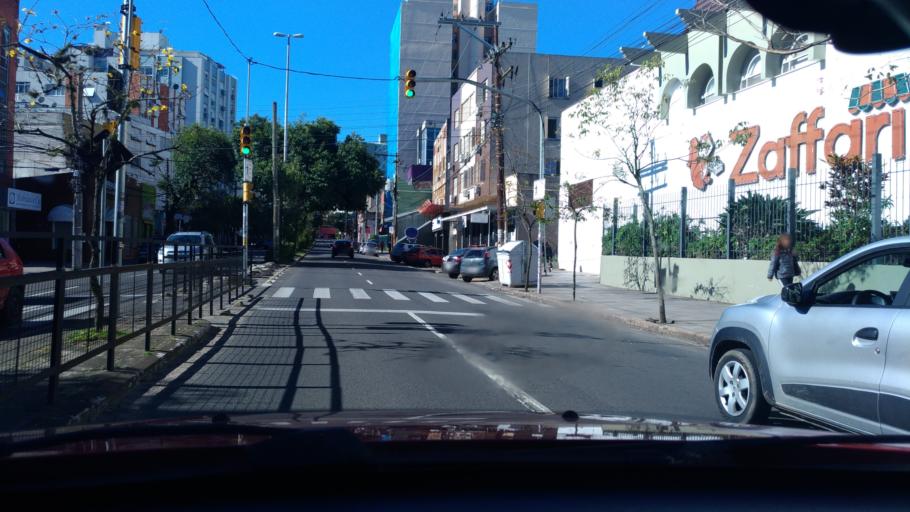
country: BR
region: Rio Grande do Sul
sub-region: Porto Alegre
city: Porto Alegre
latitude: -30.0206
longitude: -51.2073
